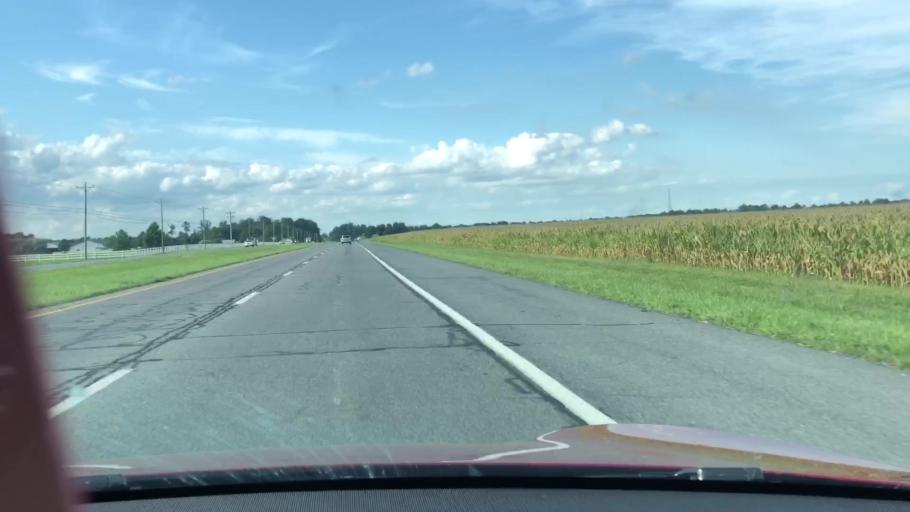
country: US
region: Delaware
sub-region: Kent County
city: Harrington
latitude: 38.9548
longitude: -75.5643
